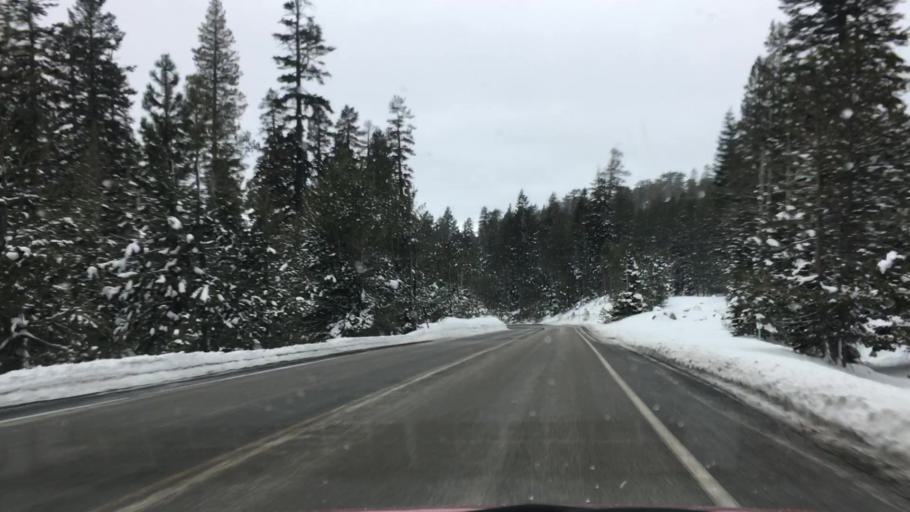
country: US
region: California
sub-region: El Dorado County
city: South Lake Tahoe
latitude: 38.7056
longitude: -120.1095
